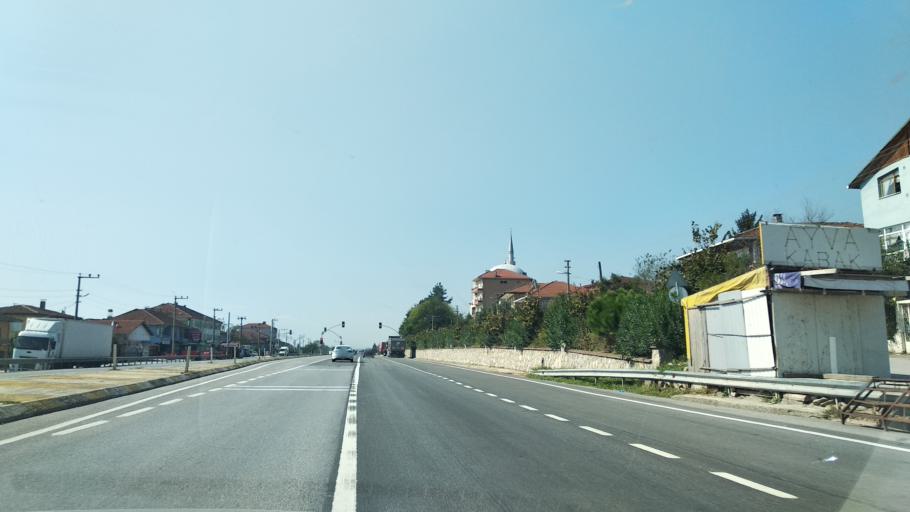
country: TR
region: Sakarya
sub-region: Merkez
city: Sapanca
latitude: 40.7339
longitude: 30.2225
